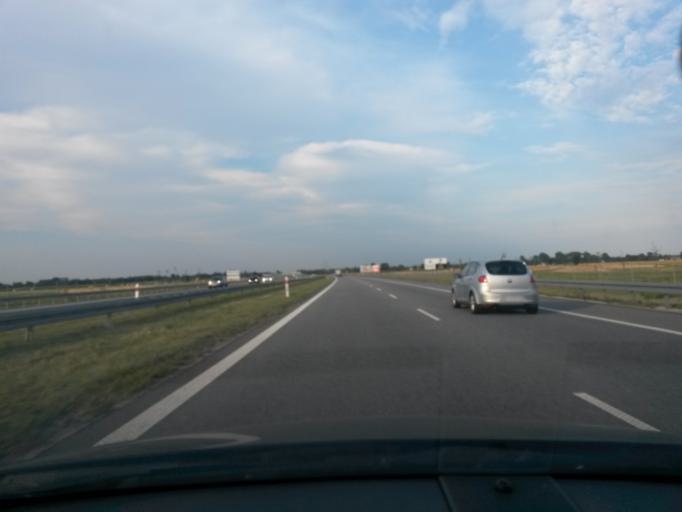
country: PL
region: Lodz Voivodeship
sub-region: powiat Lowicki
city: Lyszkowice
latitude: 52.0029
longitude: 19.9437
